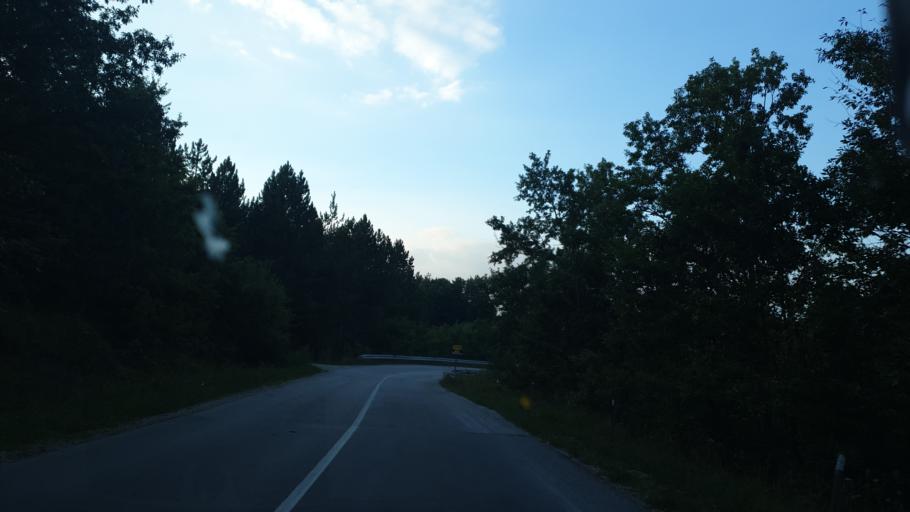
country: RS
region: Central Serbia
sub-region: Zlatiborski Okrug
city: Kosjeric
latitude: 44.0307
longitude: 20.0114
